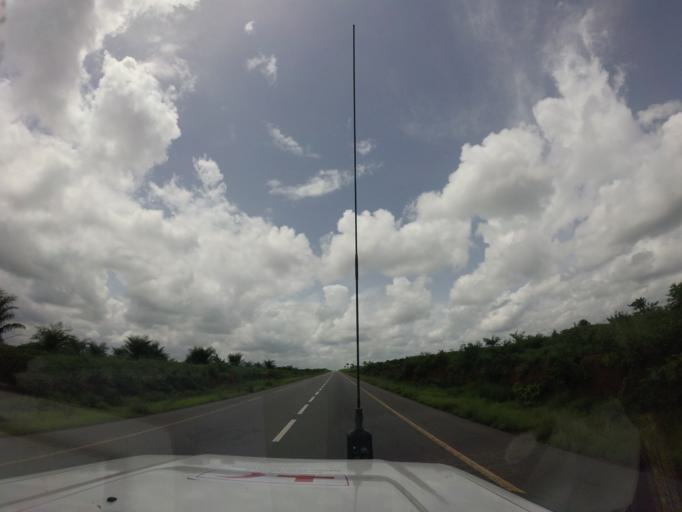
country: SL
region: Northern Province
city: Mange
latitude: 8.8660
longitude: -12.8113
